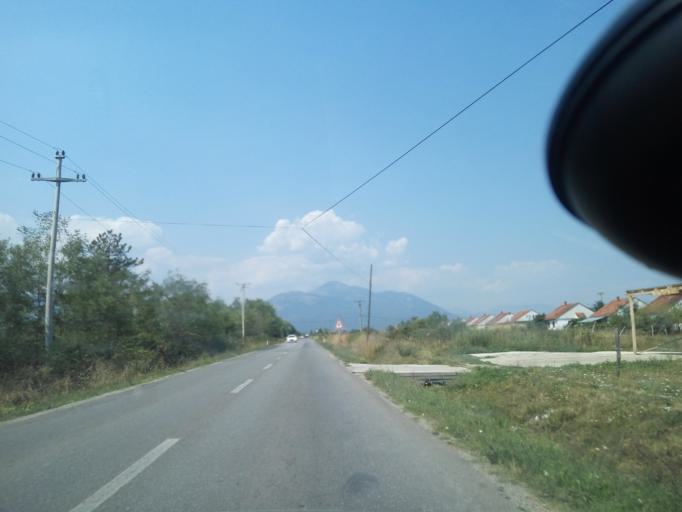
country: XK
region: Gjakova
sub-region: Komuna e Decanit
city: Prilep
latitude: 42.4763
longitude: 20.3377
